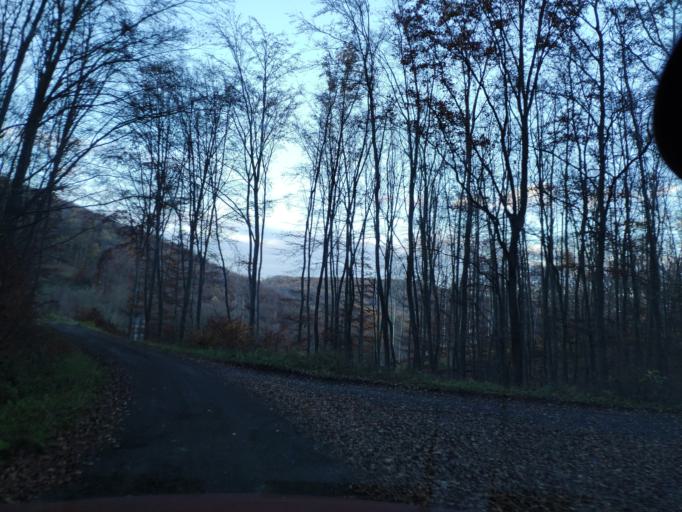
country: SK
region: Kosicky
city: Secovce
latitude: 48.5954
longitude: 21.5111
